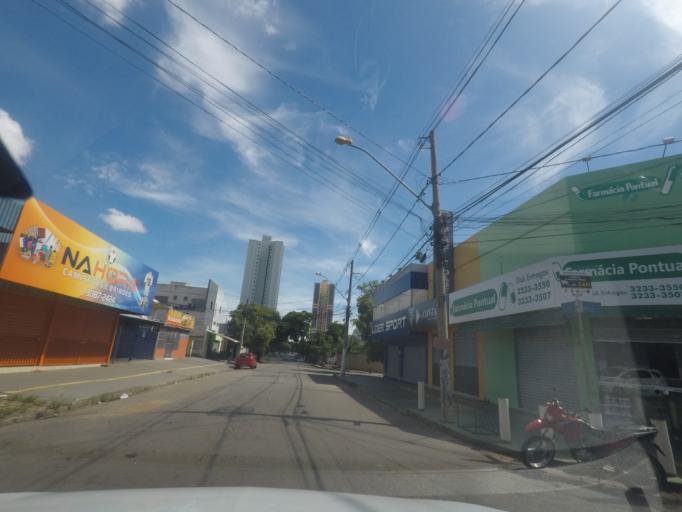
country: BR
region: Goias
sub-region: Goiania
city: Goiania
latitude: -16.6754
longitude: -49.2784
